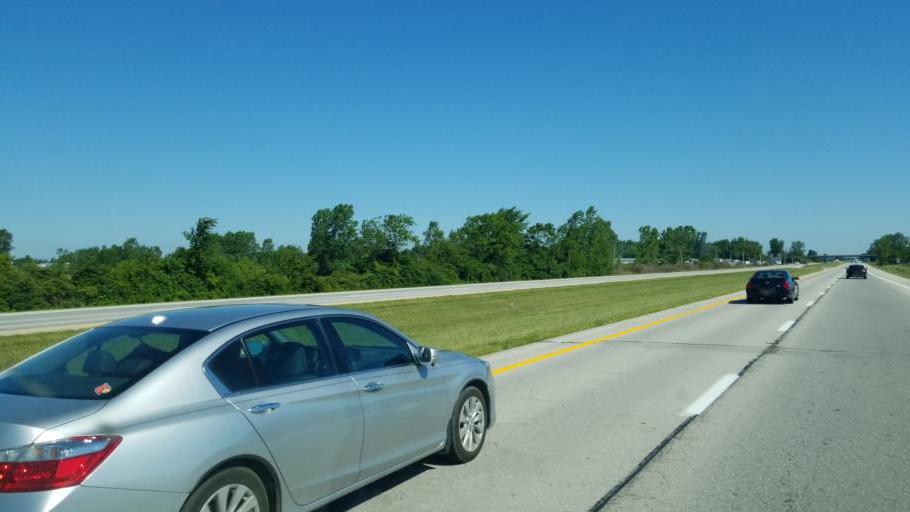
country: US
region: Ohio
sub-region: Marion County
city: Marion
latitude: 40.6227
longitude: -83.0957
